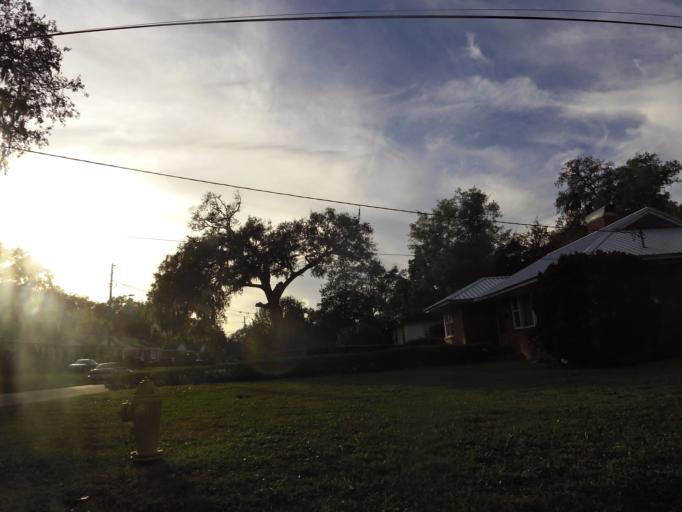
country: US
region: Florida
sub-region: Duval County
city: Jacksonville
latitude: 30.3907
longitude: -81.6589
